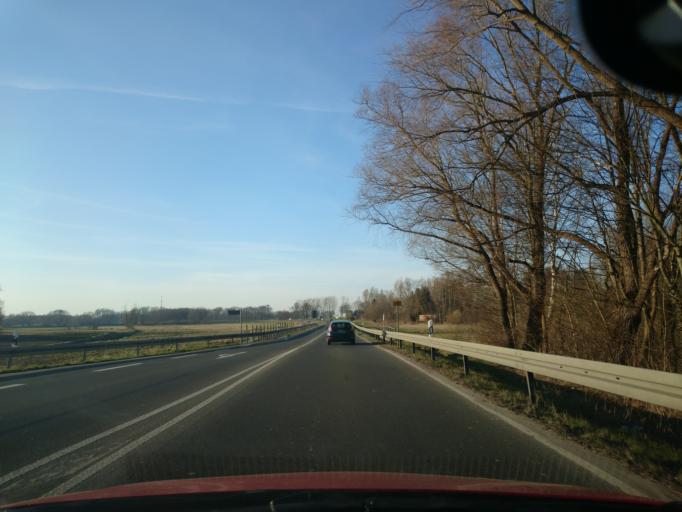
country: DE
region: Mecklenburg-Vorpommern
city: Brandshagen
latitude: 54.2116
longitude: 13.2473
